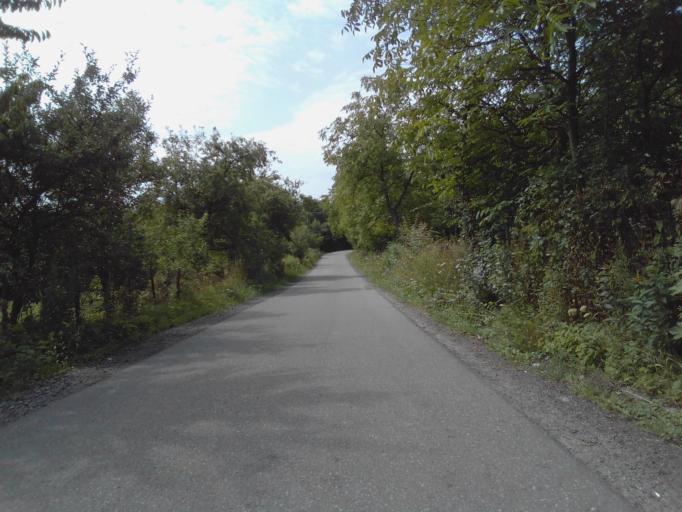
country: PL
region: Subcarpathian Voivodeship
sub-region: Powiat jasielski
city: Jaslo
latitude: 49.8066
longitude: 21.5069
